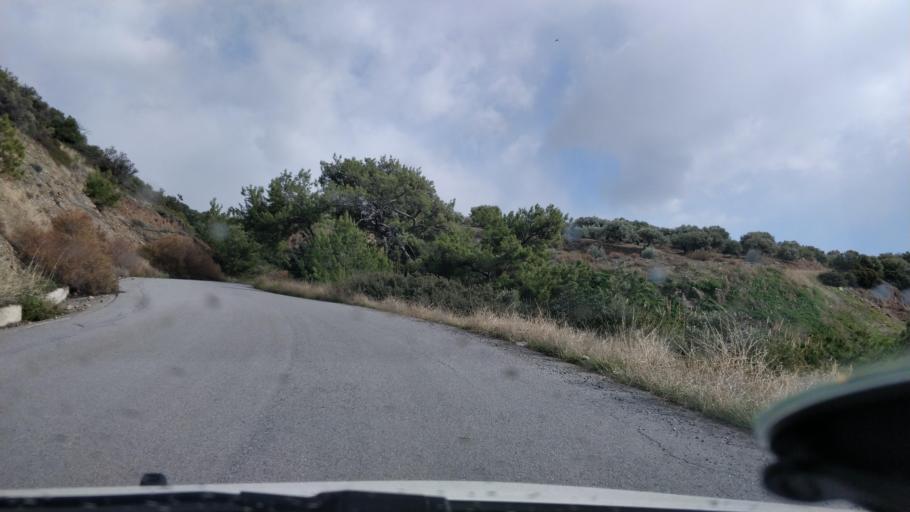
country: GR
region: Crete
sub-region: Nomos Lasithiou
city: Gra Liyia
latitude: 34.9952
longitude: 25.5104
